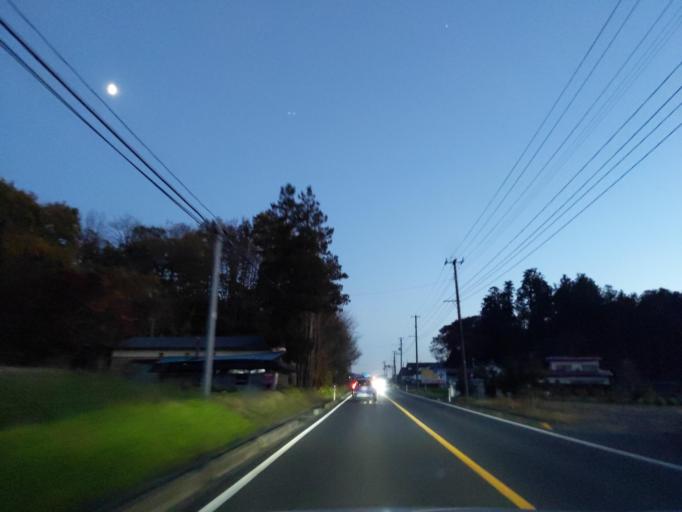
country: JP
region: Fukushima
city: Sukagawa
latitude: 37.3410
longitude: 140.4058
